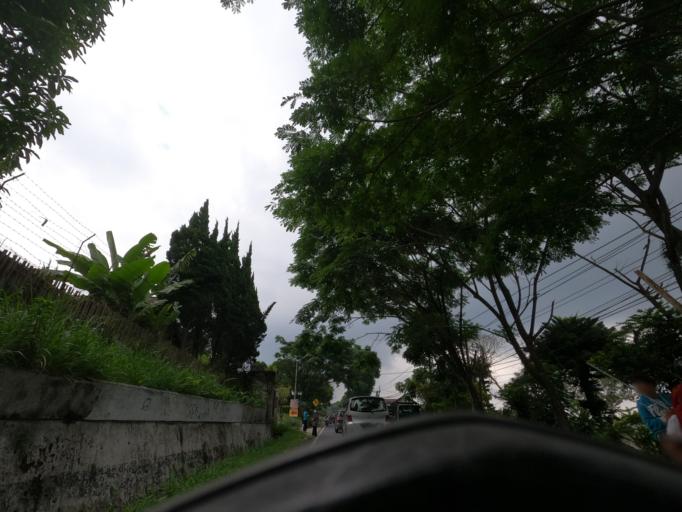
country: ID
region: West Java
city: Sukabumi
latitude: -6.7660
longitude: 107.0554
